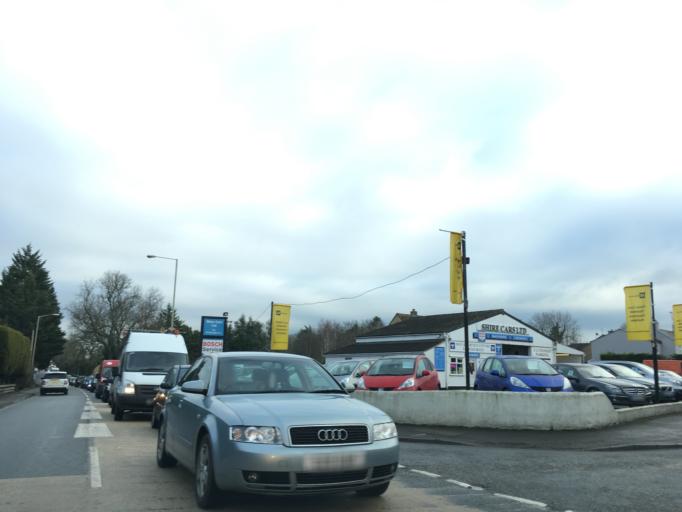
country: GB
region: England
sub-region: Gloucestershire
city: Shurdington
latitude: 51.8678
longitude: -2.1119
